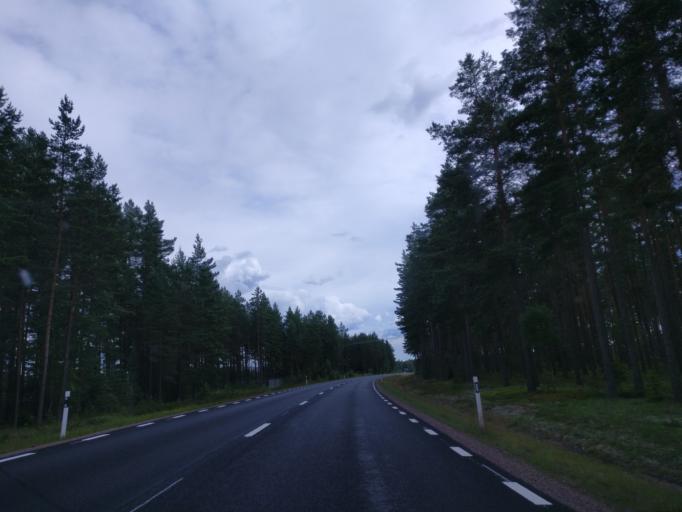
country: SE
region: Vaermland
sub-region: Hagfors Kommun
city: Hagfors
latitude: 60.0410
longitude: 13.5848
